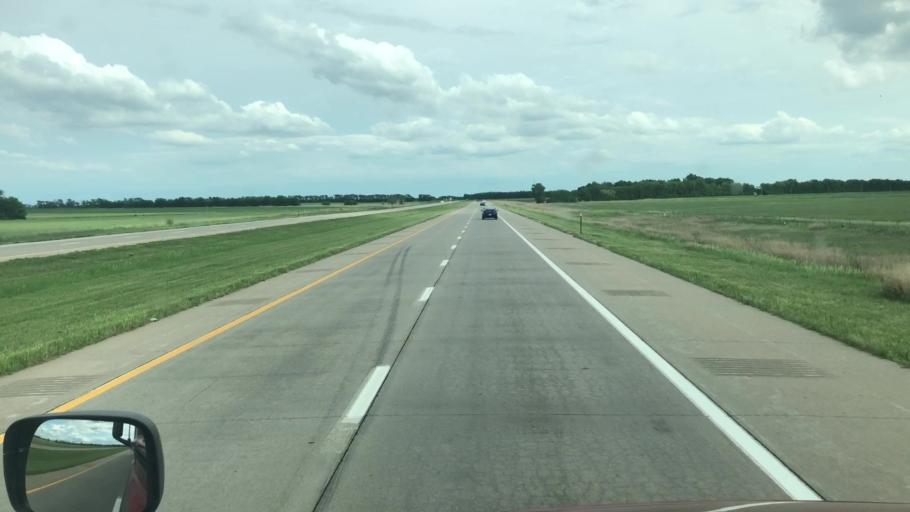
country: US
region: Kansas
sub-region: McPherson County
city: Moundridge
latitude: 38.2644
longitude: -97.5592
